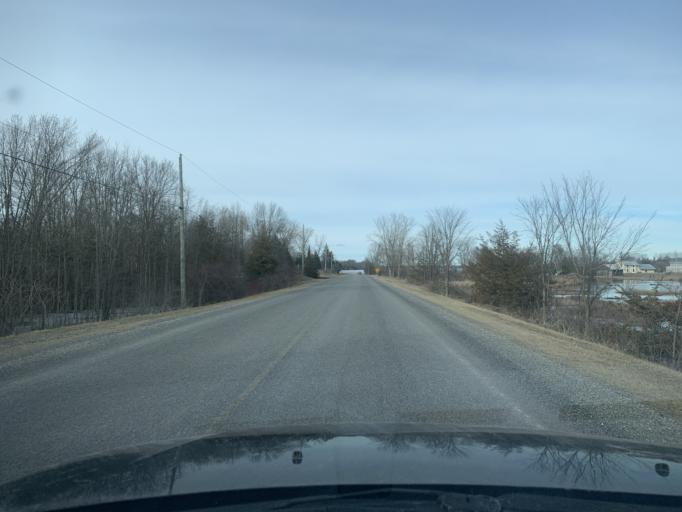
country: CA
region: Ontario
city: Greater Napanee
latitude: 44.4737
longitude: -77.0469
